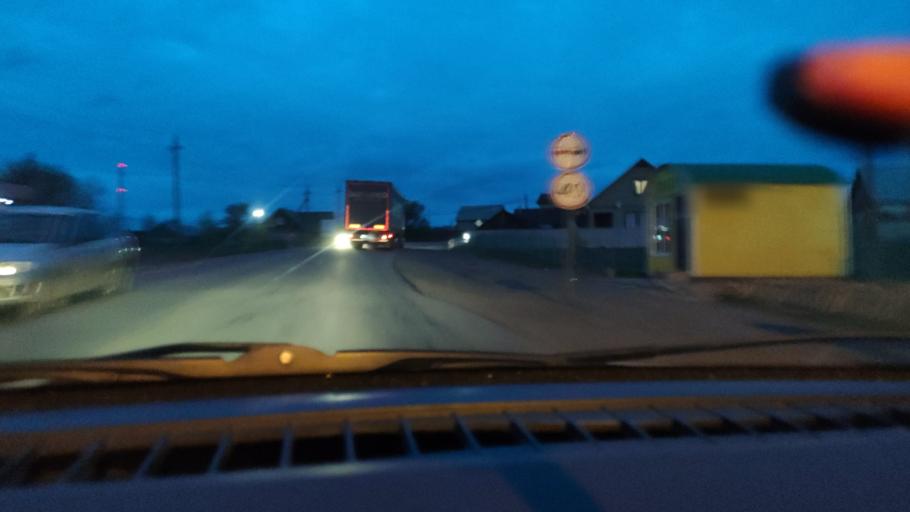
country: RU
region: Orenburg
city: Tatarskaya Kargala
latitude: 51.9477
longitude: 55.1761
